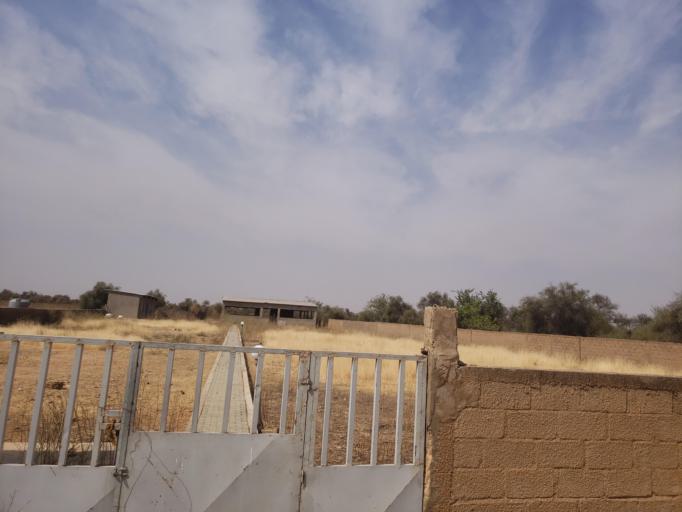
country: SN
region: Matam
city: Ranerou
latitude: 15.2901
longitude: -13.9649
